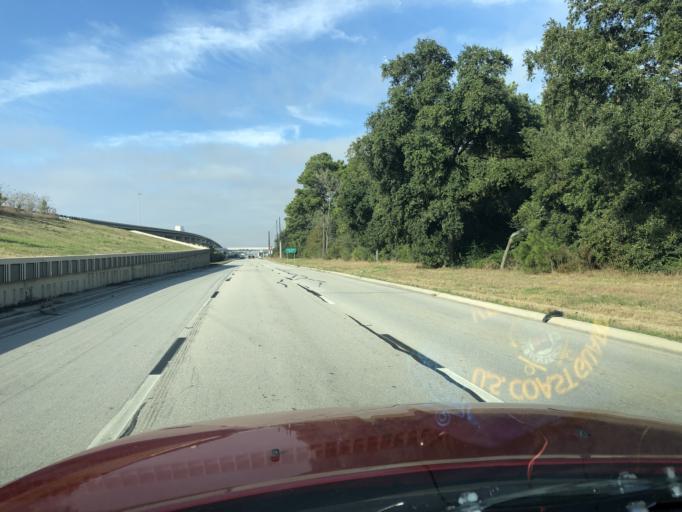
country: US
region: Texas
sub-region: Harris County
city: Tomball
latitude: 30.0523
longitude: -95.6103
